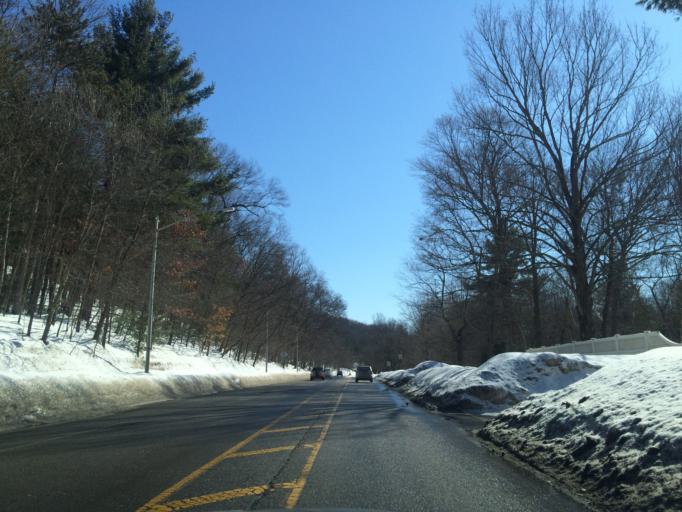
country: US
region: Massachusetts
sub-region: Norfolk County
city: Wellesley
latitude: 42.2980
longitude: -71.2779
